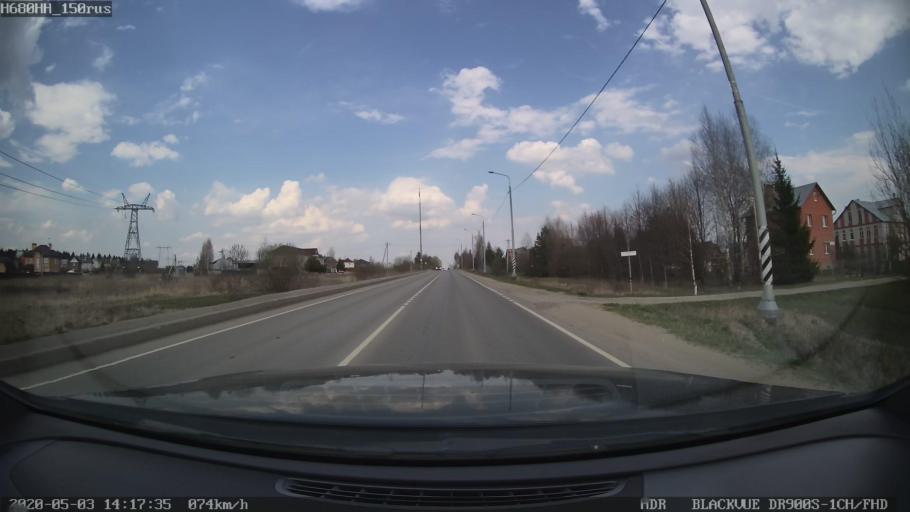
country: RU
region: Moskovskaya
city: Solnechnogorsk
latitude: 56.2102
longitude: 36.9662
